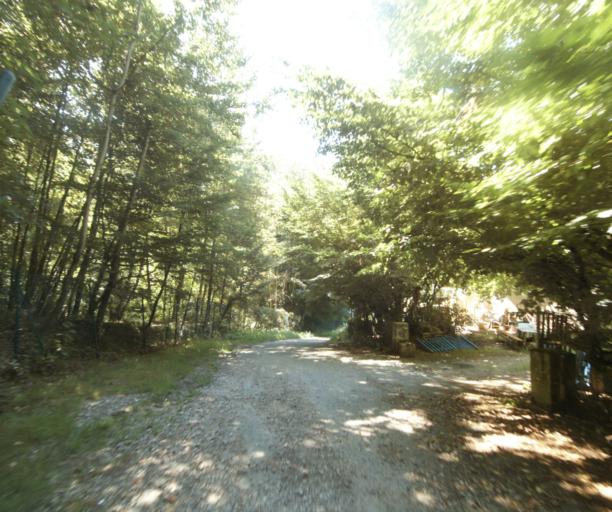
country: FR
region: Lorraine
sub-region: Departement des Vosges
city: Epinal
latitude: 48.1653
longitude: 6.4658
